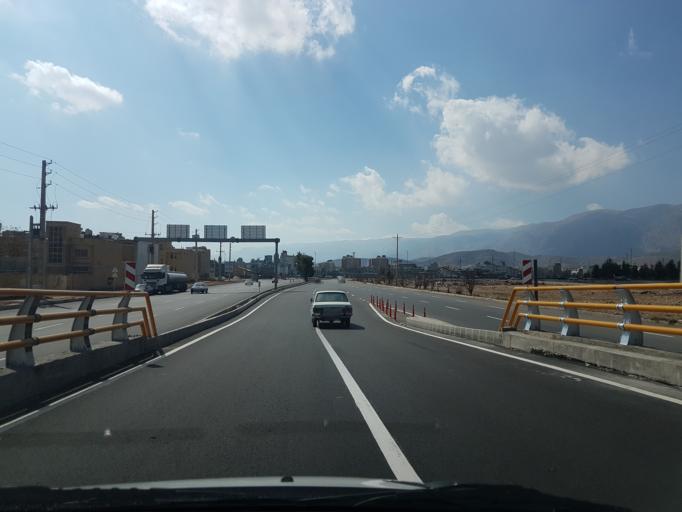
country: IR
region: Fars
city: Shiraz
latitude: 29.6102
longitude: 52.4677
